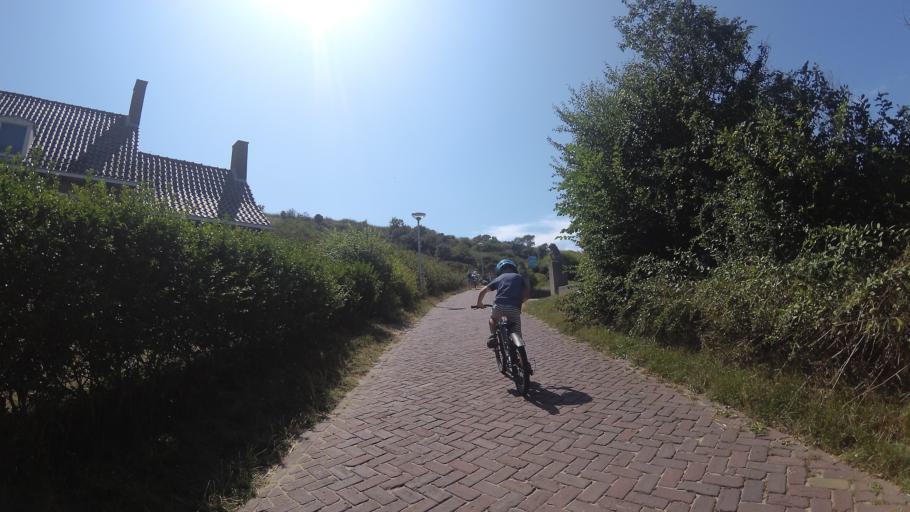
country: NL
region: Zeeland
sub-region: Gemeente Vlissingen
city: Vlissingen
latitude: 51.4985
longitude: 3.4911
